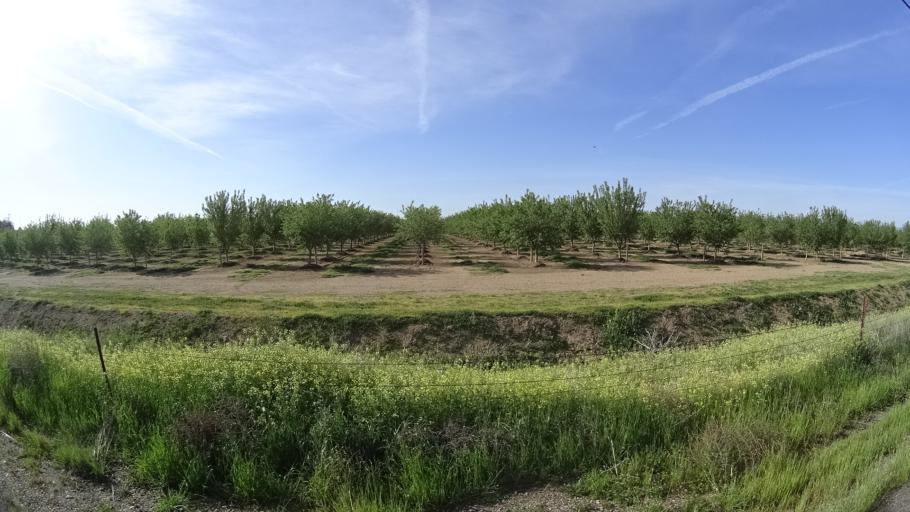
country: US
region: California
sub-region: Glenn County
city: Orland
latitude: 39.6683
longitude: -122.2555
